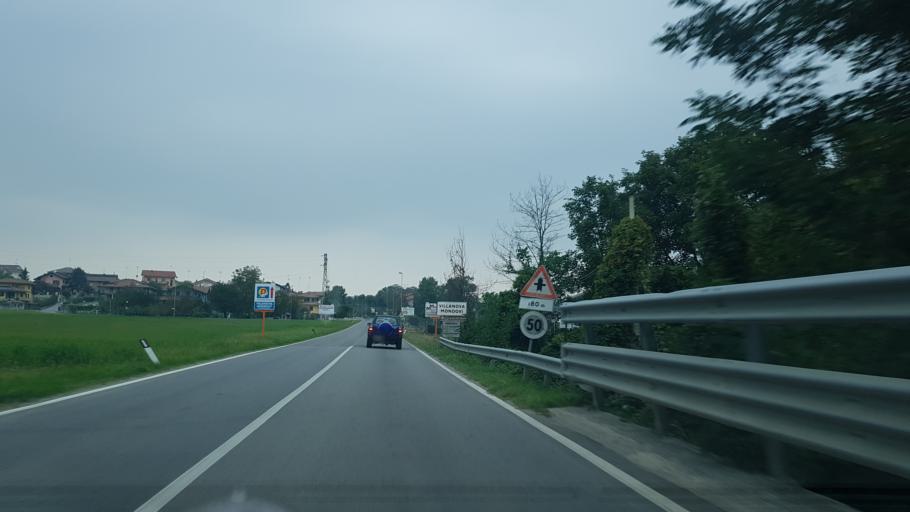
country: IT
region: Piedmont
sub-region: Provincia di Cuneo
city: Villanova Mondovi
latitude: 44.3413
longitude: 7.7778
